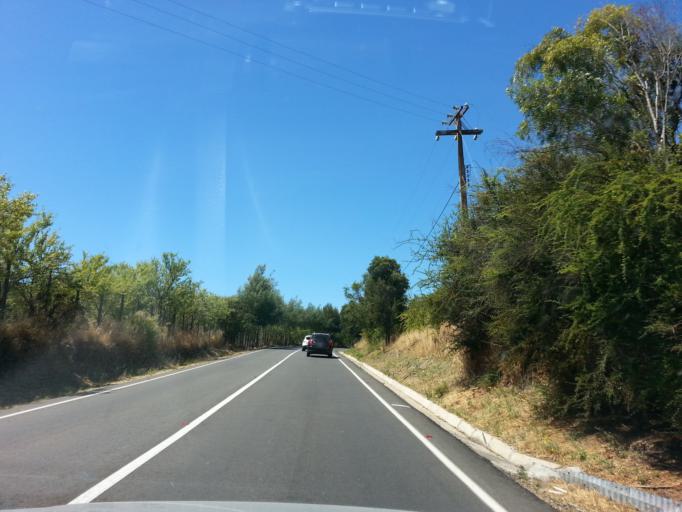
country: CL
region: Valparaiso
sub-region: Provincia de Marga Marga
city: Villa Alemana
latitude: -33.2026
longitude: -71.3804
